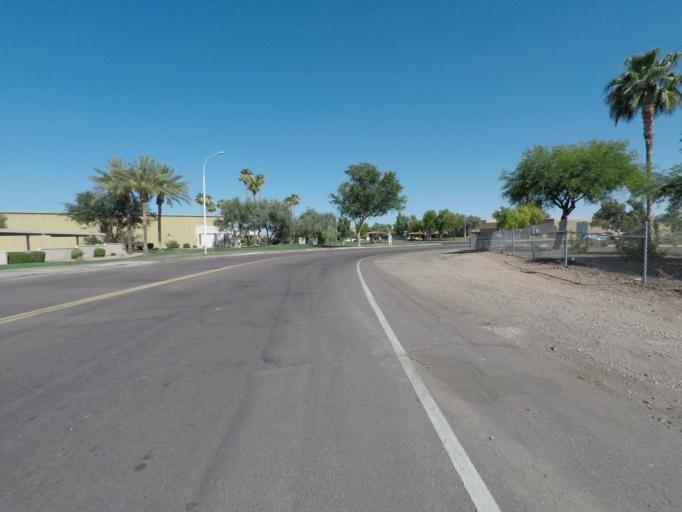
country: US
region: Arizona
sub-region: Maricopa County
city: Tempe Junction
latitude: 33.4225
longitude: -111.9766
